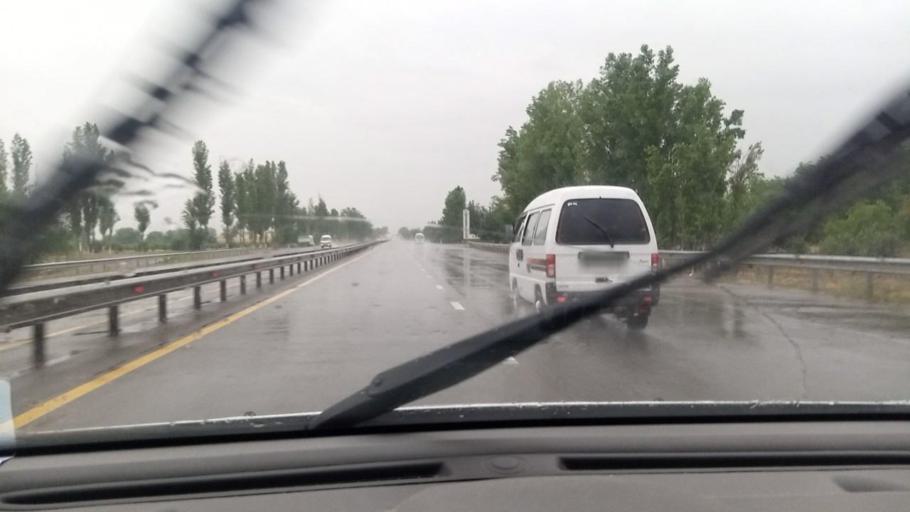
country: UZ
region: Toshkent
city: Tuytepa
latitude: 41.1186
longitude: 69.4431
